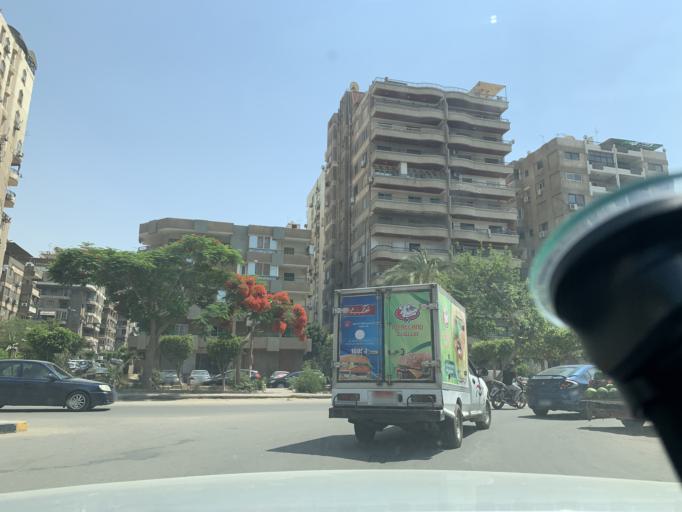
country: EG
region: Muhafazat al Qahirah
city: Cairo
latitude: 30.0611
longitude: 31.3496
